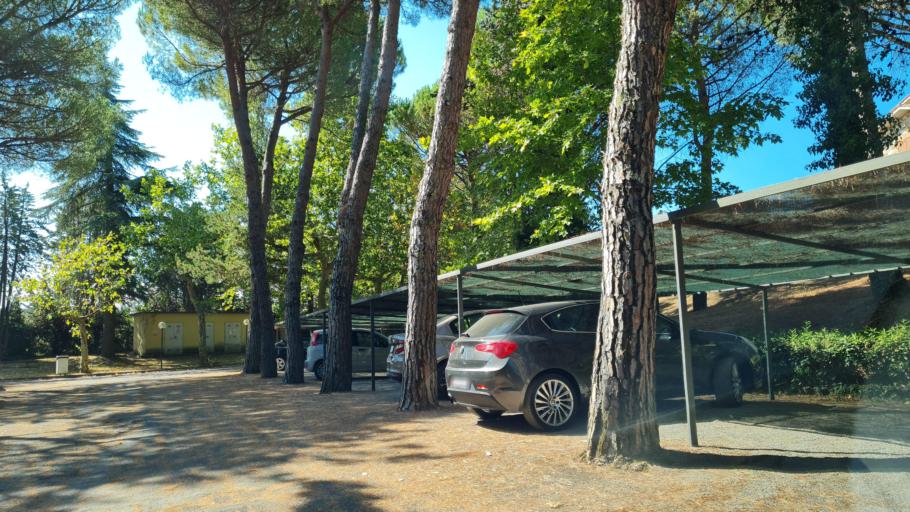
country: IT
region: Tuscany
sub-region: Provincia di Siena
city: Chianciano Terme
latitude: 43.0409
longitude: 11.8099
